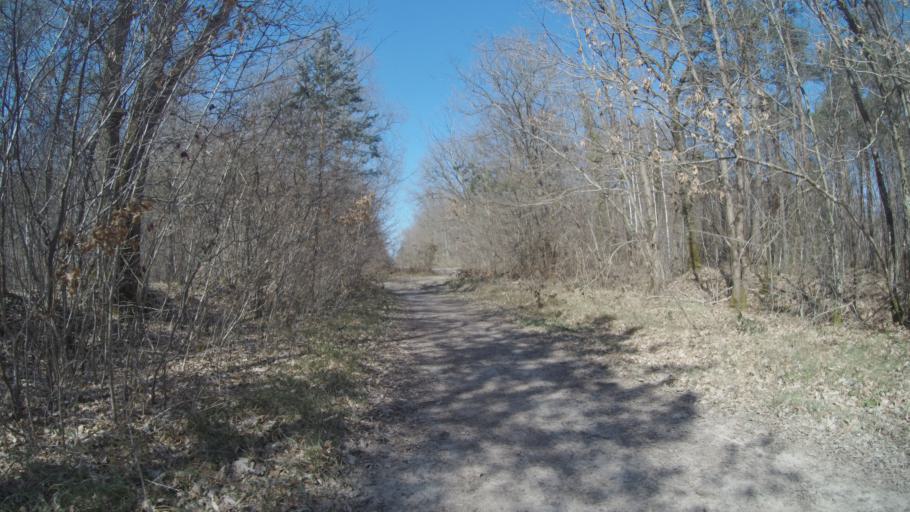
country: FR
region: Centre
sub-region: Departement du Loiret
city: Chanteau
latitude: 47.9491
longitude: 1.9820
